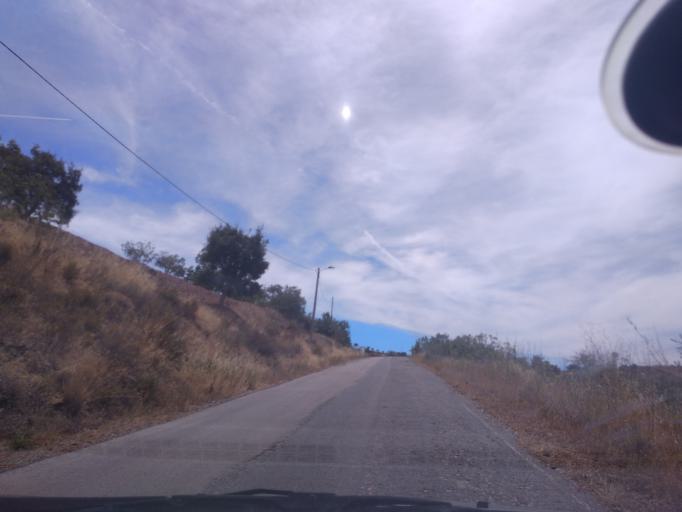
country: PT
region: Faro
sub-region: Sao Bras de Alportel
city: Sao Bras de Alportel
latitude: 37.1751
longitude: -7.8062
